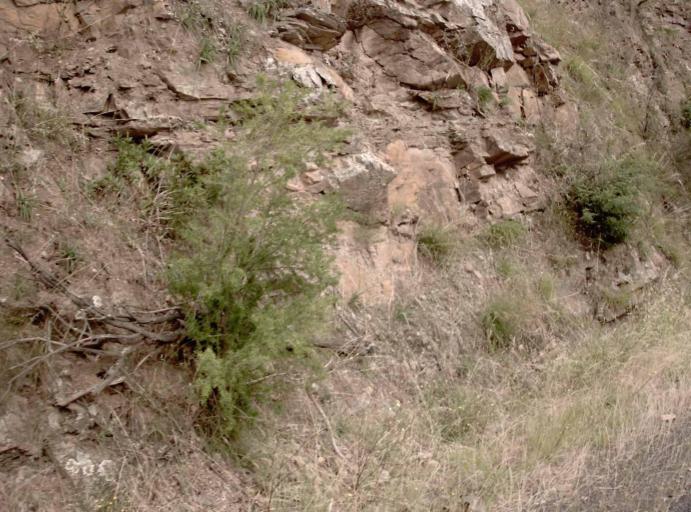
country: AU
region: Victoria
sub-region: Wellington
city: Heyfield
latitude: -37.7725
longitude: 146.6664
